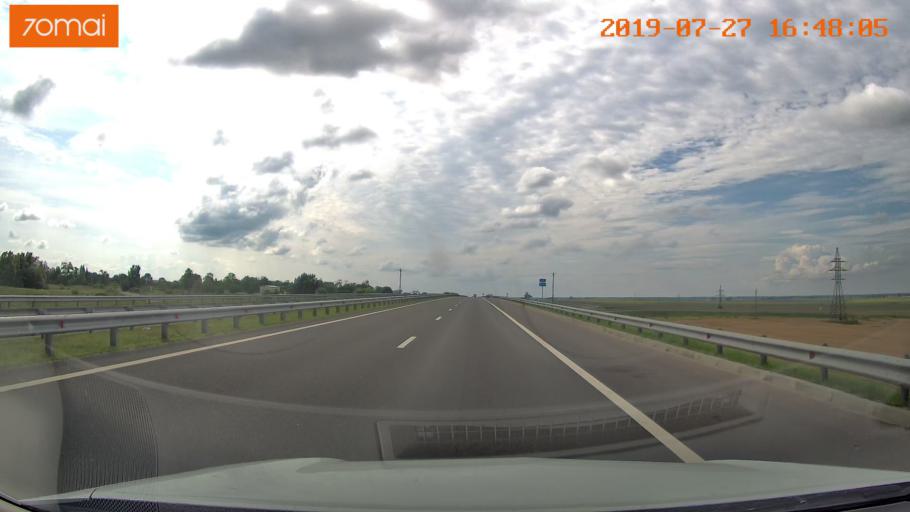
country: RU
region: Kaliningrad
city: Gvardeysk
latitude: 54.6695
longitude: 20.9771
